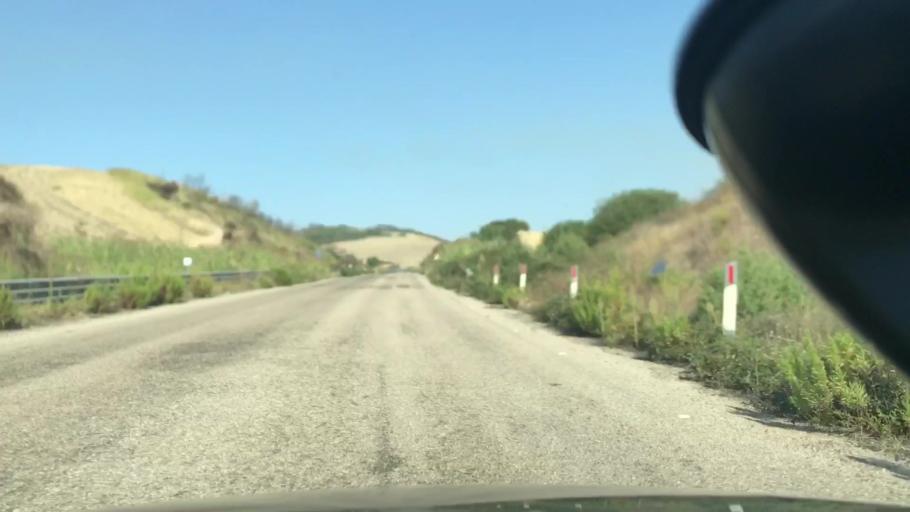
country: IT
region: Basilicate
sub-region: Provincia di Matera
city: Grottole
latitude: 40.6959
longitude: 16.4244
